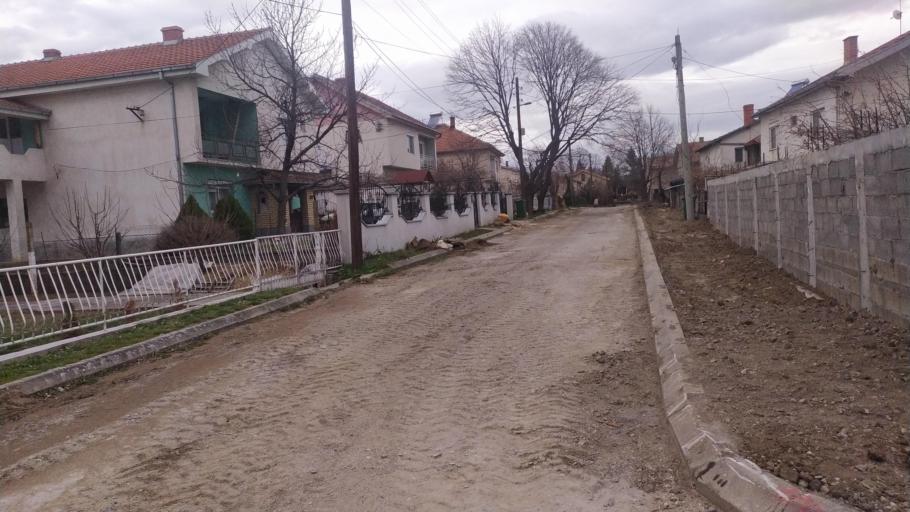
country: MK
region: Demir Kapija
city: Demir Kapija
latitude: 41.4131
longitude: 22.2393
